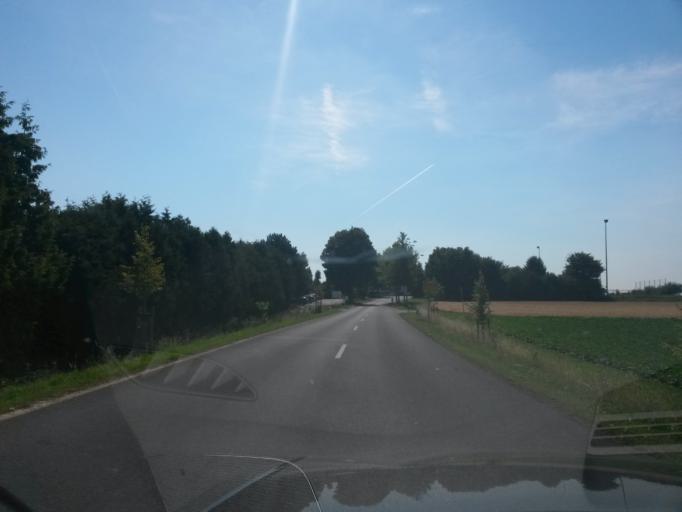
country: DE
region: Bavaria
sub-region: Regierungsbezirk Unterfranken
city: Estenfeld
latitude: 49.8344
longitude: 9.9951
